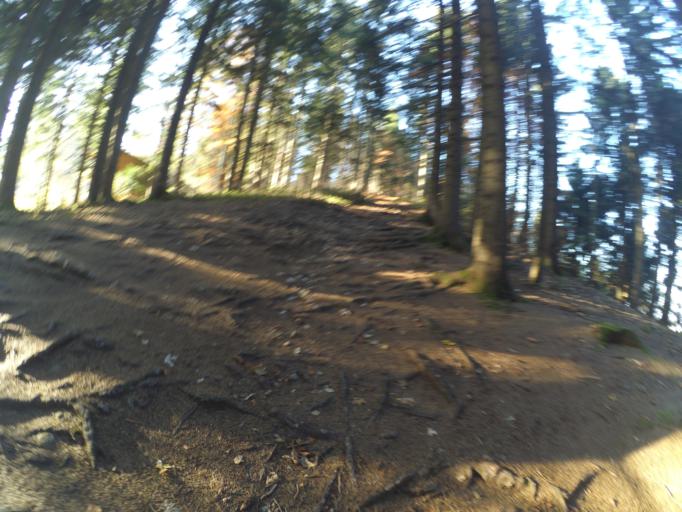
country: DE
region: Bavaria
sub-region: Upper Bavaria
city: Bernbeuren
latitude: 47.7325
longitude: 10.7435
